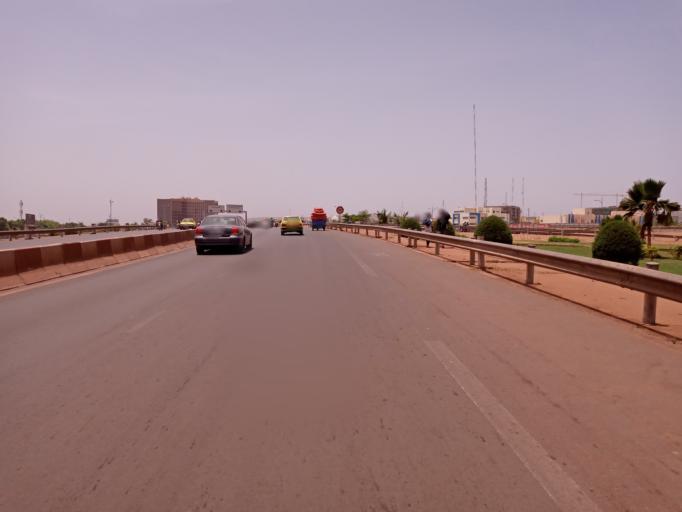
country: ML
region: Bamako
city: Bamako
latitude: 12.6326
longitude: -8.0102
